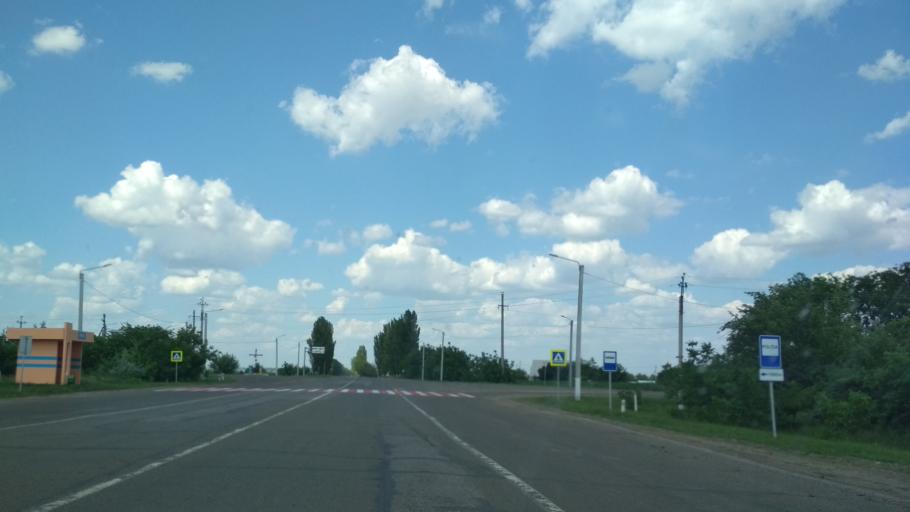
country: MD
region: Chisinau
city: Vadul lui Voda
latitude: 47.1186
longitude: 29.1101
